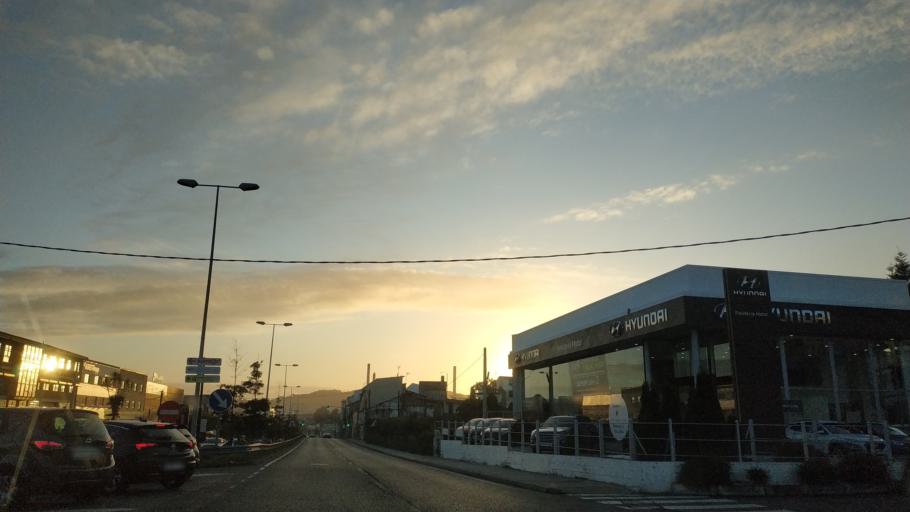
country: ES
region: Galicia
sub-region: Provincia da Coruna
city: A Coruna
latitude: 43.3569
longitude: -8.4252
